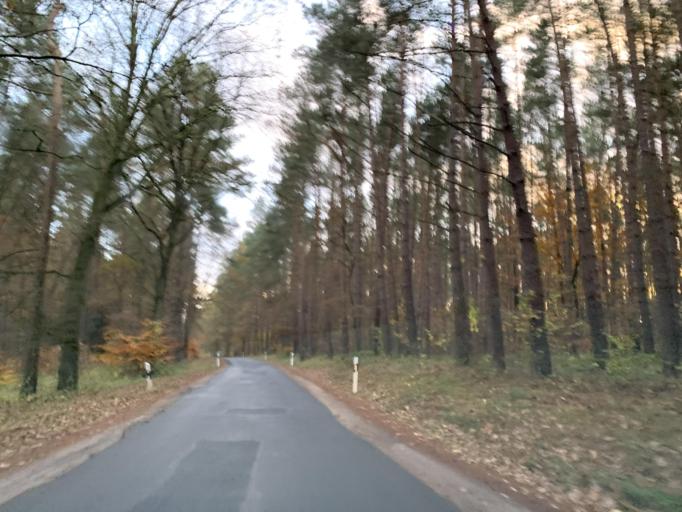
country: DE
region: Mecklenburg-Vorpommern
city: Blankensee
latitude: 53.3969
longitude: 13.2617
